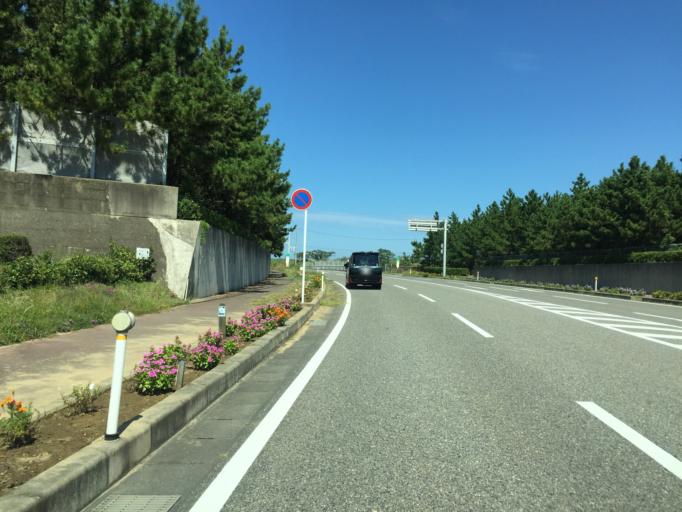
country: JP
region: Niigata
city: Niigata-shi
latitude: 37.9415
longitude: 139.0584
